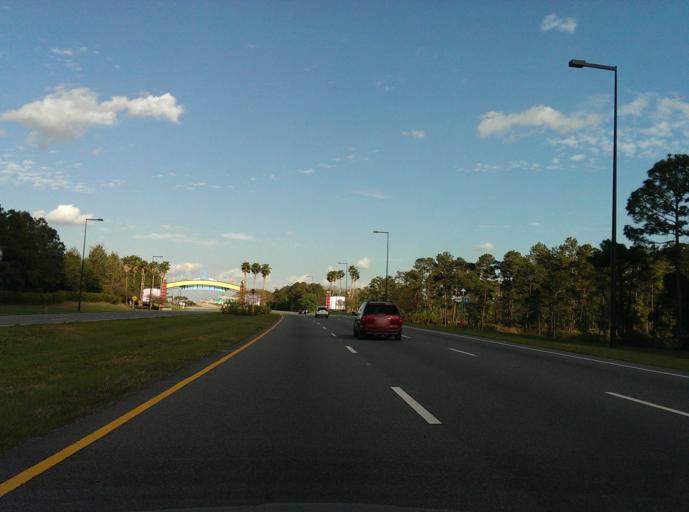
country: US
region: Florida
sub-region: Osceola County
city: Celebration
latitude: 28.3461
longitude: -81.5464
